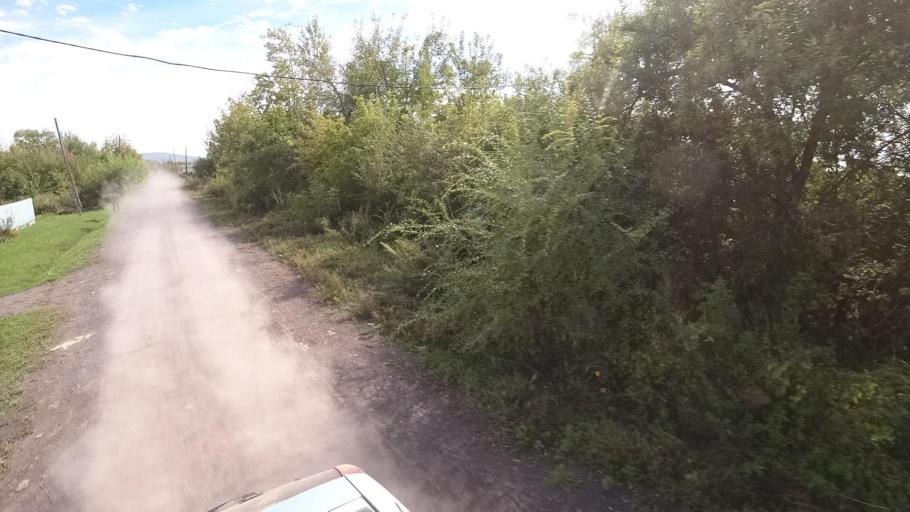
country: RU
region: Primorskiy
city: Yakovlevka
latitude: 44.4350
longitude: 133.5655
